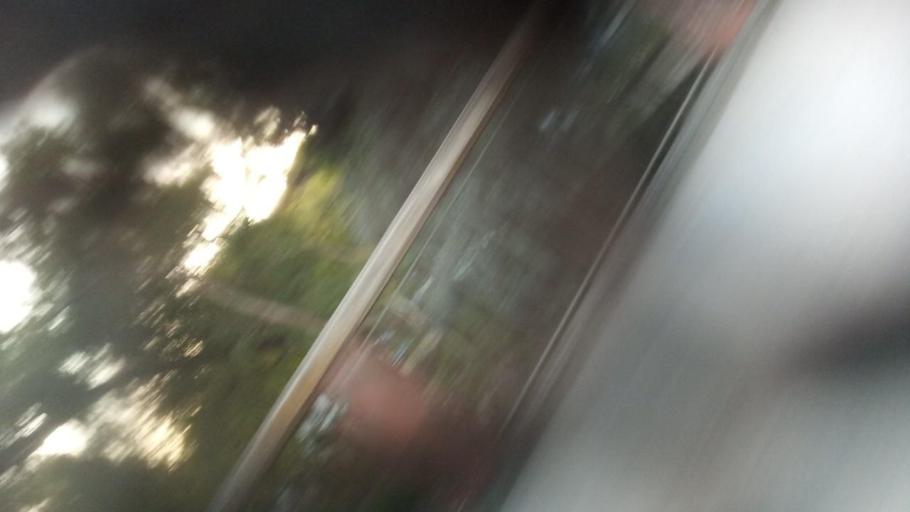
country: AR
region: Jujuy
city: San Salvador de Jujuy
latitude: -24.1895
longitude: -65.3104
